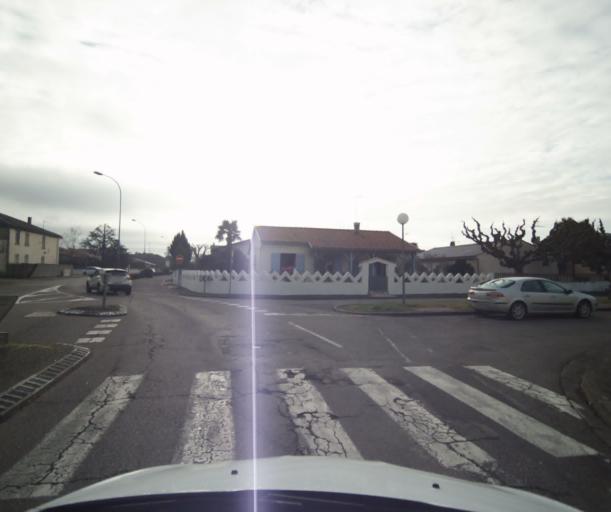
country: FR
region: Midi-Pyrenees
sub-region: Departement du Tarn-et-Garonne
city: Castelsarrasin
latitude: 44.0465
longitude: 1.0990
